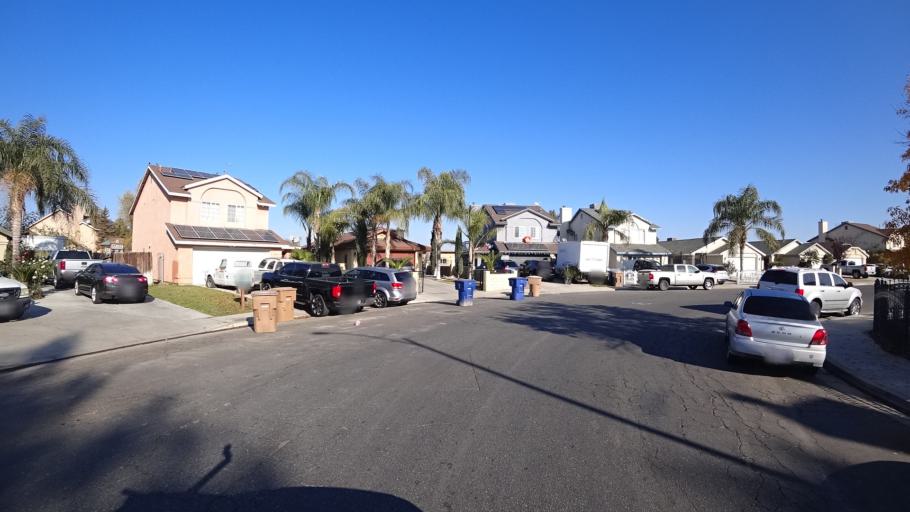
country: US
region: California
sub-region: Kern County
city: Greenfield
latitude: 35.3061
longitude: -119.0154
